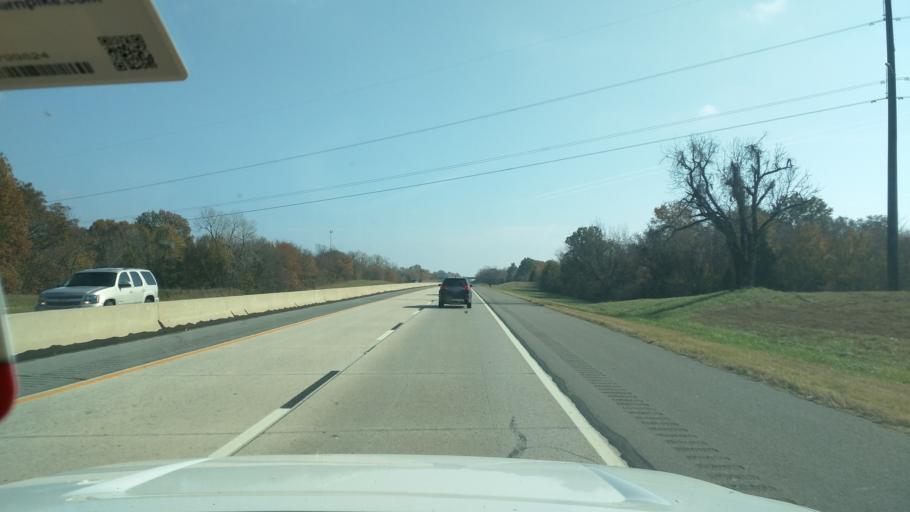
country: US
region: Oklahoma
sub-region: Muskogee County
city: Muskogee
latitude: 35.8308
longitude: -95.3576
